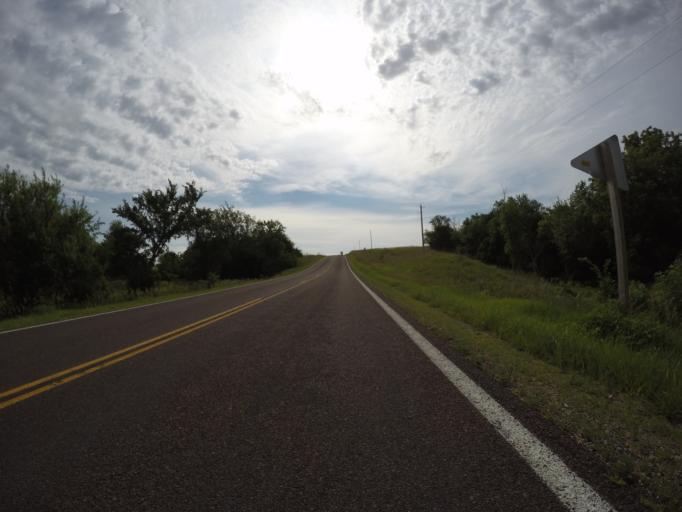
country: US
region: Kansas
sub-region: Republic County
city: Belleville
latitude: 39.7122
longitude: -97.3563
